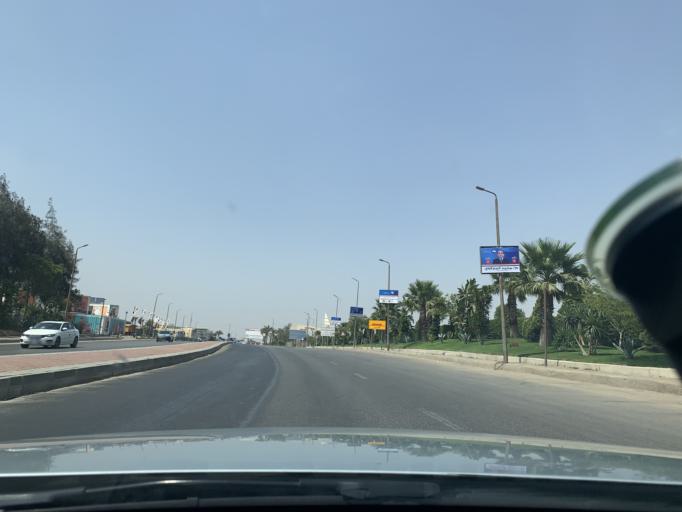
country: EG
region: Muhafazat al Qalyubiyah
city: Al Khankah
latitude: 30.0933
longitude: 31.3825
